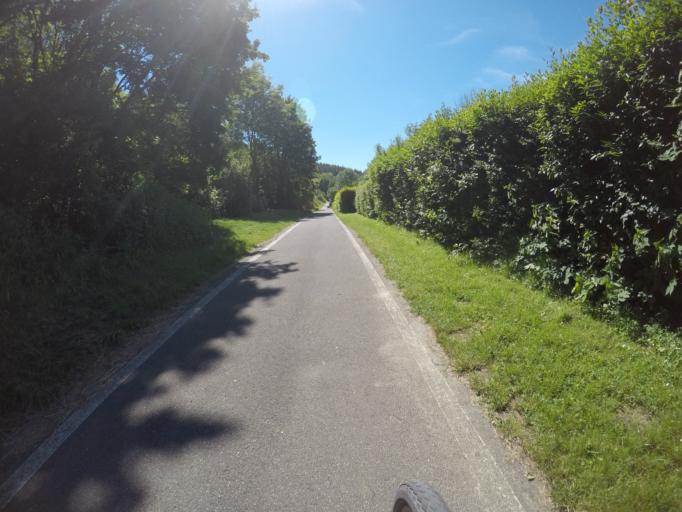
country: DE
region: Baden-Wuerttemberg
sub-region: Karlsruhe Region
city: Ispringen
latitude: 48.9275
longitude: 8.6509
